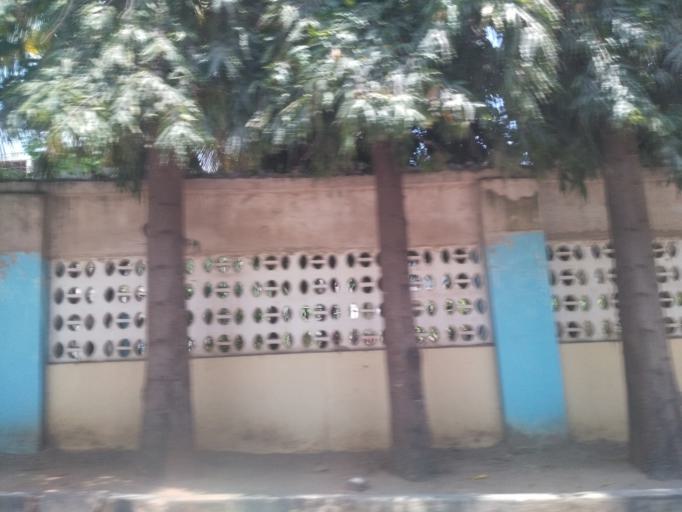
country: TZ
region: Dar es Salaam
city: Dar es Salaam
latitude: -6.7991
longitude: 39.2808
